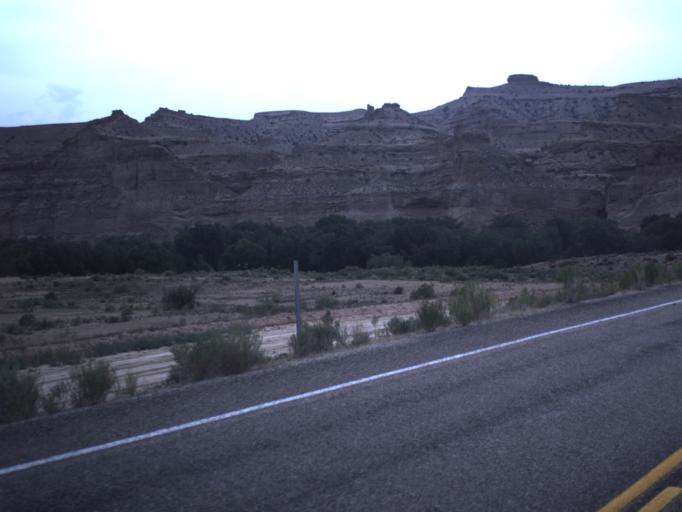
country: US
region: Colorado
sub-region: Rio Blanco County
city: Rangely
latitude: 39.9757
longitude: -109.1754
